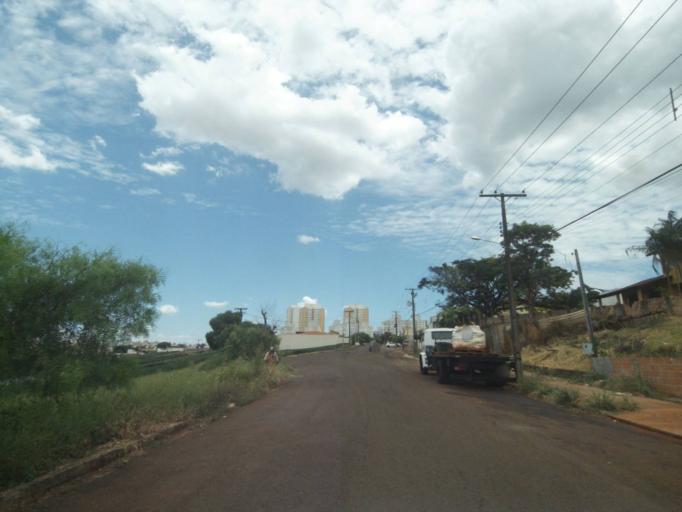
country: BR
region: Parana
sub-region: Londrina
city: Londrina
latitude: -23.3211
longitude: -51.1980
